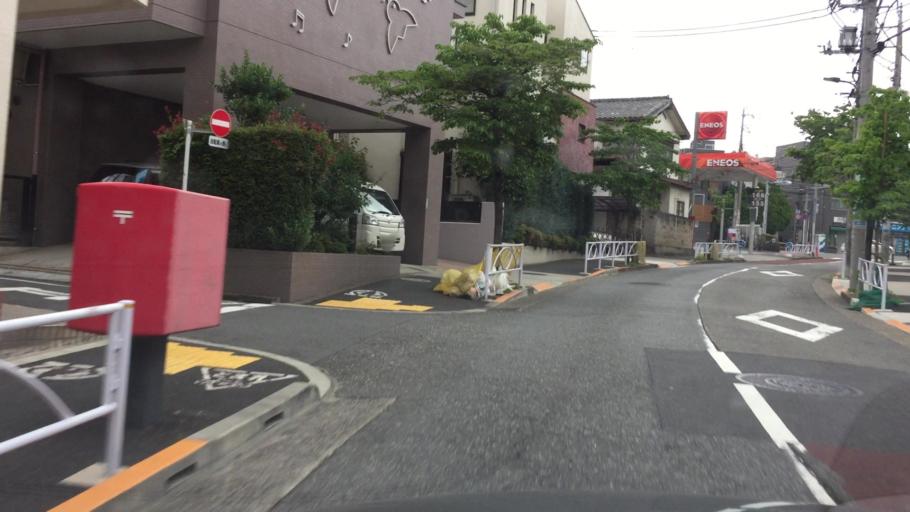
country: JP
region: Tokyo
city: Tokyo
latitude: 35.6406
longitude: 139.6866
